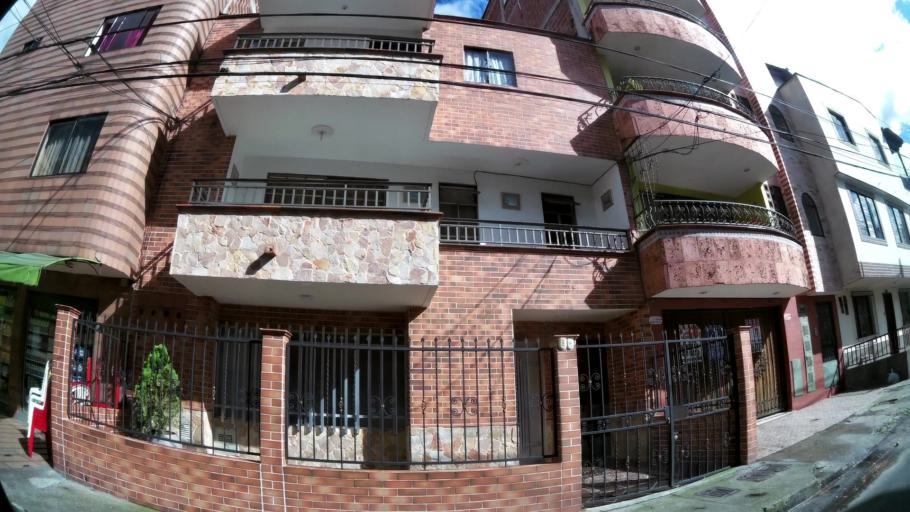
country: CO
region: Antioquia
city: Sabaneta
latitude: 6.1520
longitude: -75.6191
